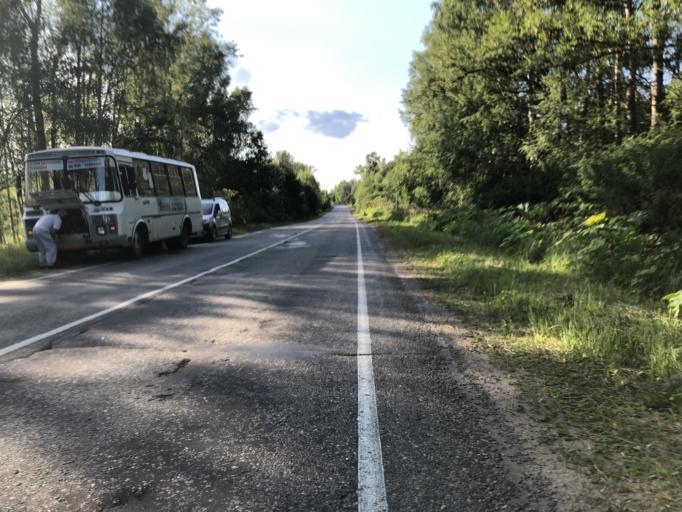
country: RU
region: Tverskaya
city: Rzhev
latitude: 56.2700
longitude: 34.2479
